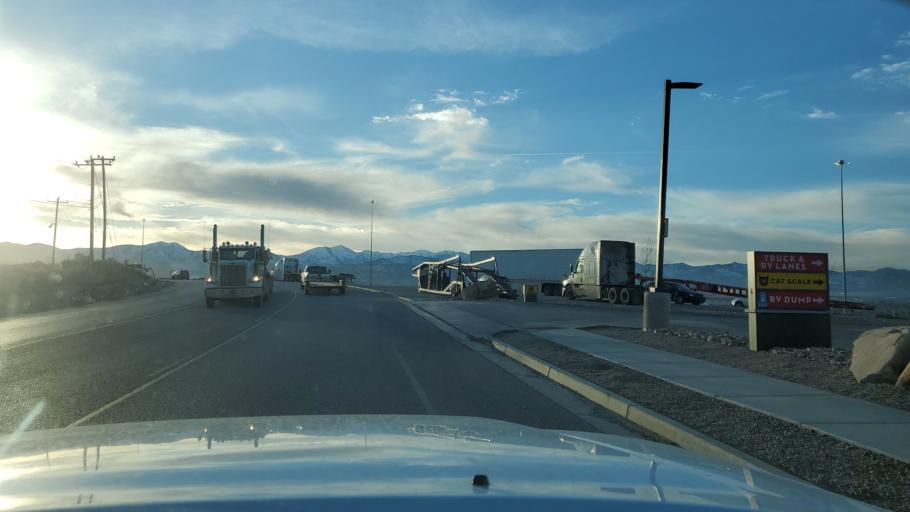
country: US
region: Utah
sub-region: Salt Lake County
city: Bluffdale
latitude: 40.4811
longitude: -111.8995
